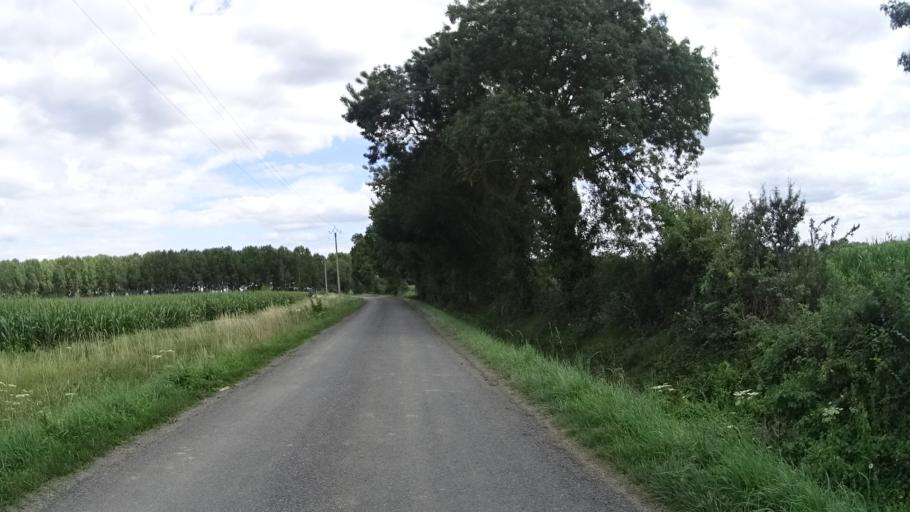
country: FR
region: Pays de la Loire
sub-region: Departement de Maine-et-Loire
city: Vivy
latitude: 47.3127
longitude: -0.0929
